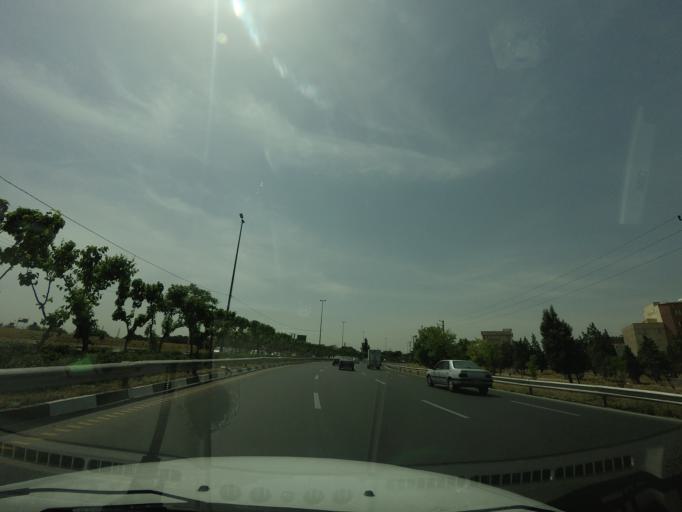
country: IR
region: Tehran
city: Eslamshahr
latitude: 35.5438
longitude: 51.2572
